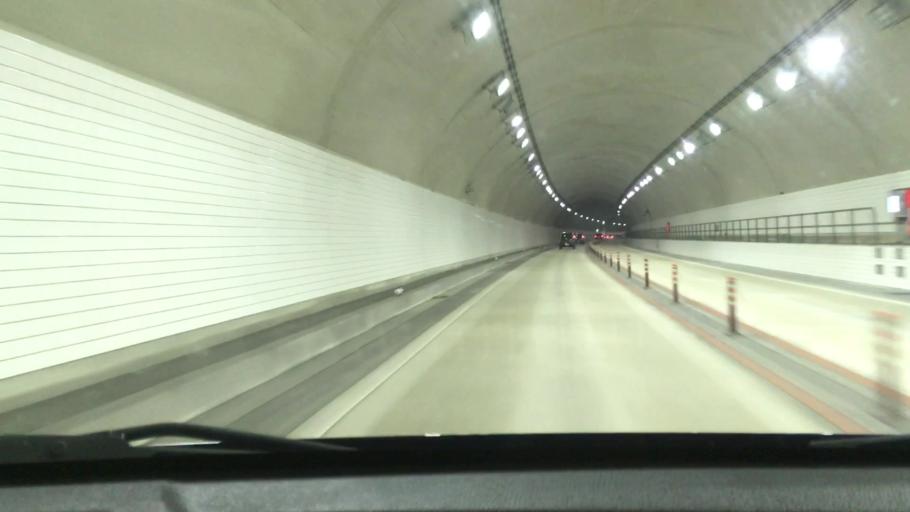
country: JP
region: Saga Prefecture
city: Karatsu
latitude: 33.3670
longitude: 129.9282
